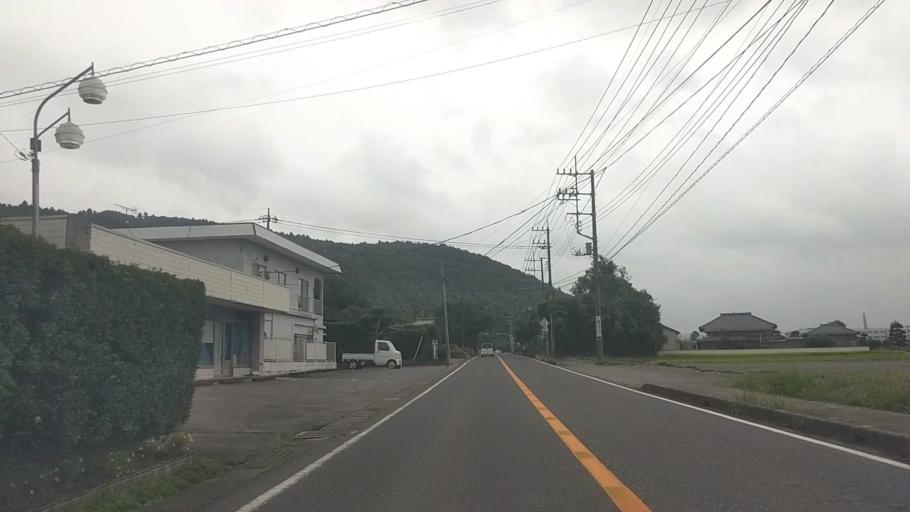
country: JP
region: Chiba
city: Kisarazu
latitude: 35.3067
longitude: 140.0688
